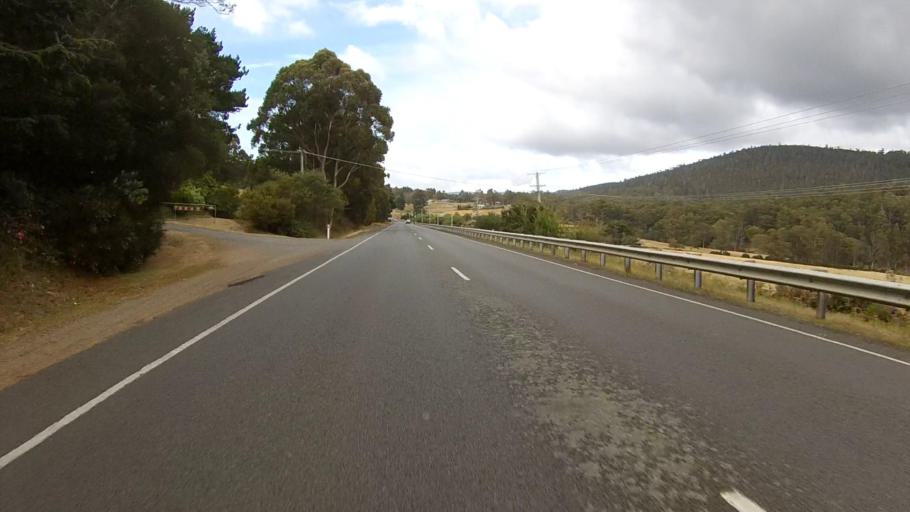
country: AU
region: Tasmania
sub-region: Kingborough
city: Kettering
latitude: -43.0813
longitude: 147.2545
